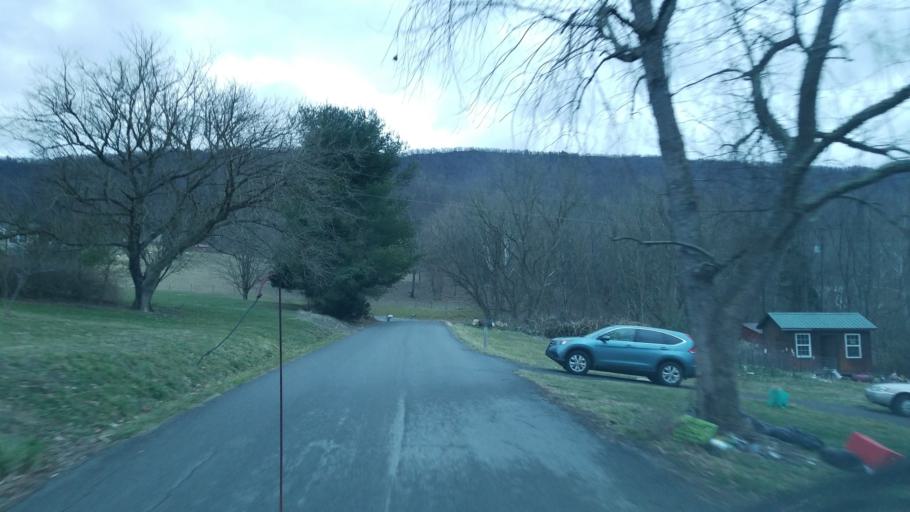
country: US
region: Virginia
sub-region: Pulaski County
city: Pulaski
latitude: 37.1591
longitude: -80.8667
